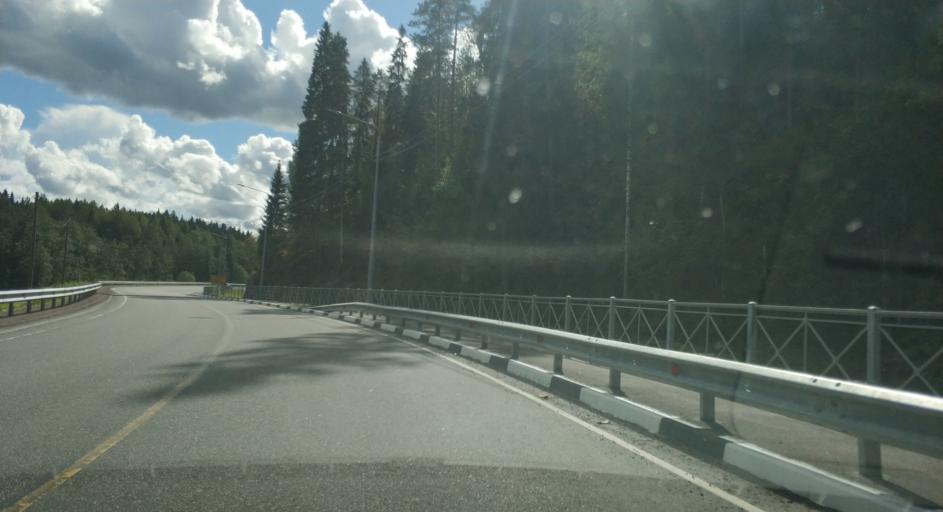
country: RU
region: Republic of Karelia
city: Ruskeala
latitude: 61.9408
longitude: 30.5911
